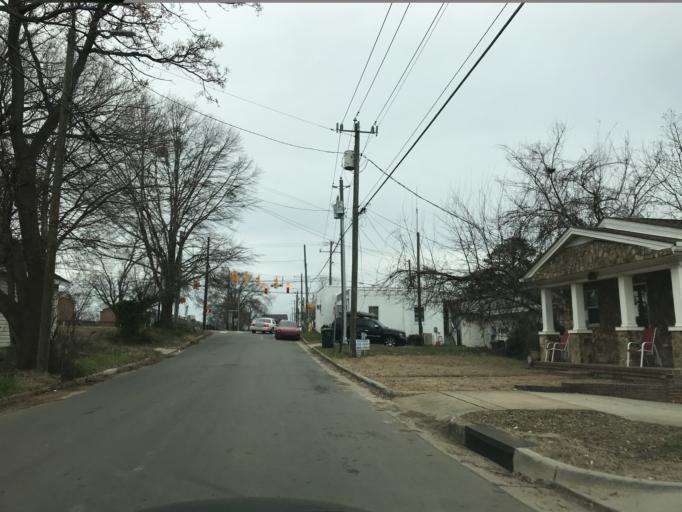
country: US
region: North Carolina
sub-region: Wake County
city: Raleigh
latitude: 35.7835
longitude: -78.6175
